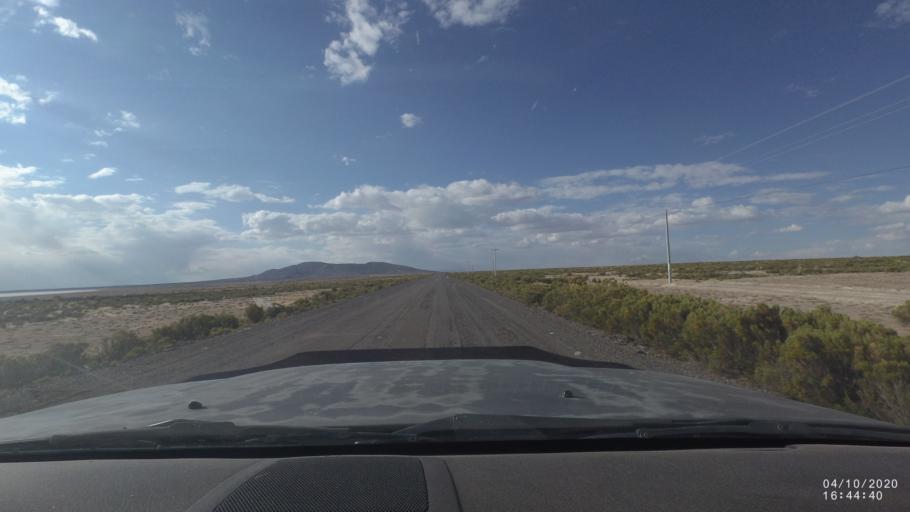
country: BO
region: Oruro
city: Poopo
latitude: -18.6806
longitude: -67.5600
